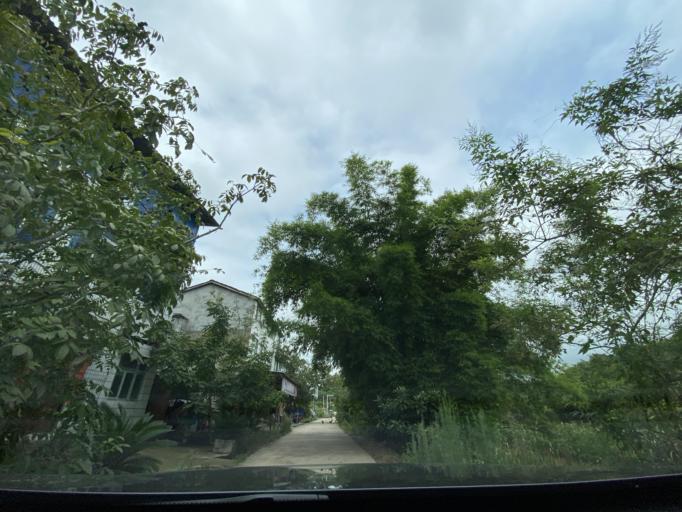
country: CN
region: Sichuan
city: Jiancheng
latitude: 30.4002
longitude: 104.5676
